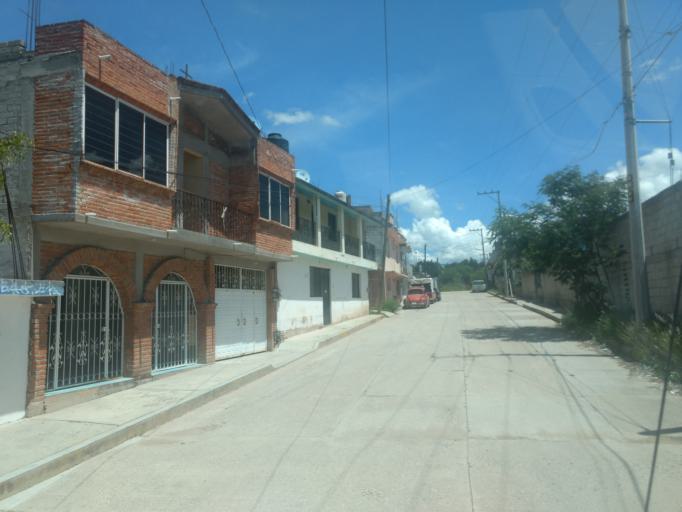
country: MX
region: Oaxaca
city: Ciudad de Huajuapam de Leon
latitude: 17.8151
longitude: -97.7910
